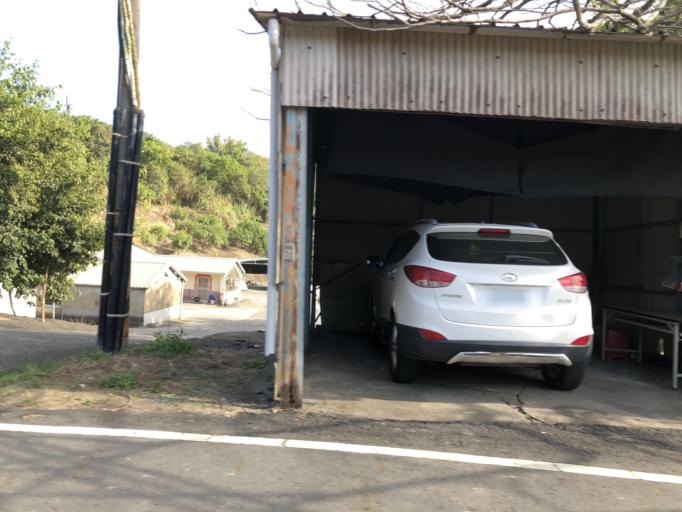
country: TW
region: Taiwan
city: Yujing
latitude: 23.0345
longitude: 120.3971
